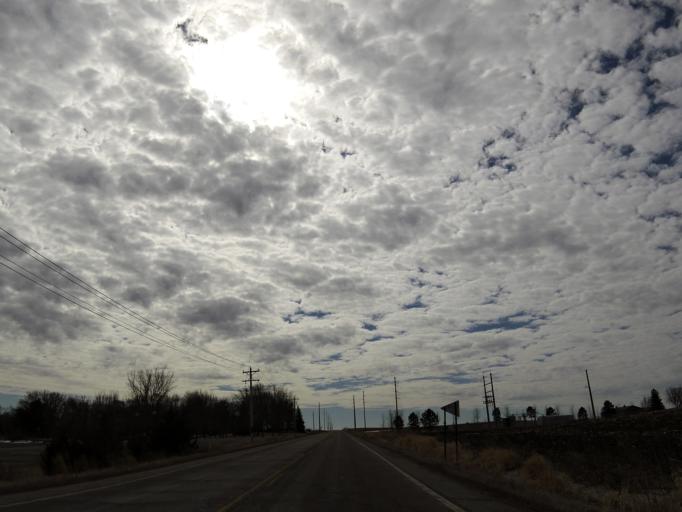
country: US
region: Minnesota
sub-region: Scott County
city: Jordan
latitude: 44.6401
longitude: -93.5627
